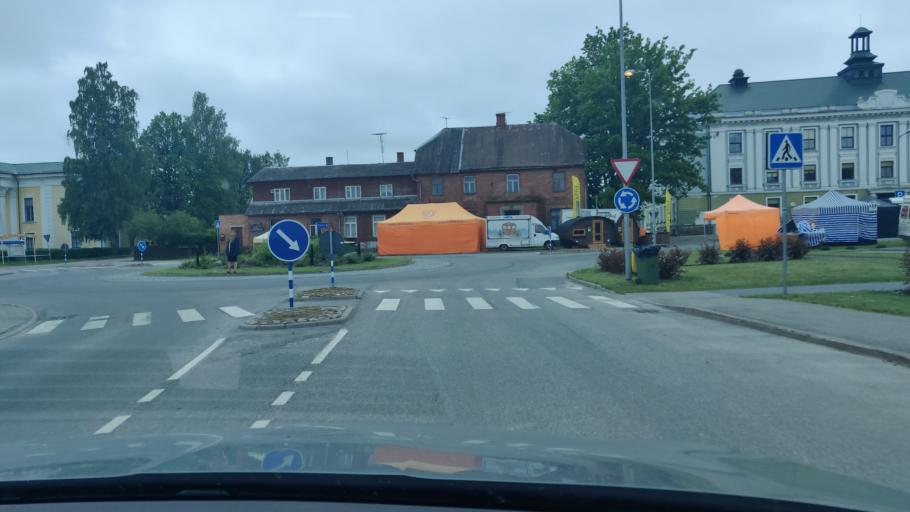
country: EE
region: Vorumaa
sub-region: Voru linn
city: Voru
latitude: 57.7323
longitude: 27.2833
